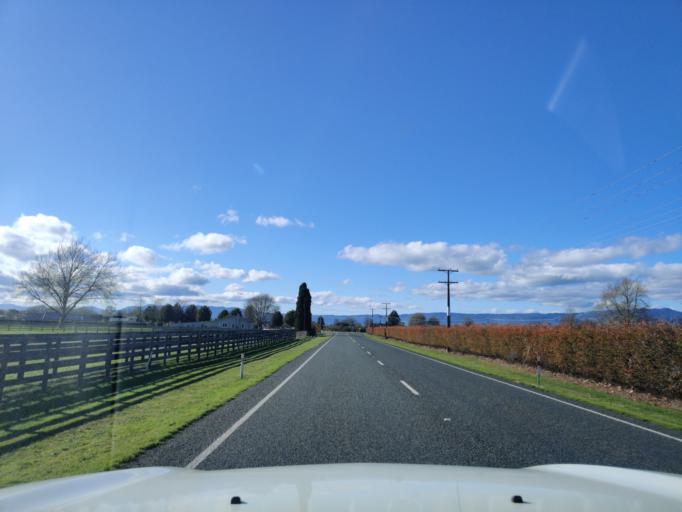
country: NZ
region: Waikato
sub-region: Matamata-Piako District
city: Matamata
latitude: -37.8655
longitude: 175.7520
